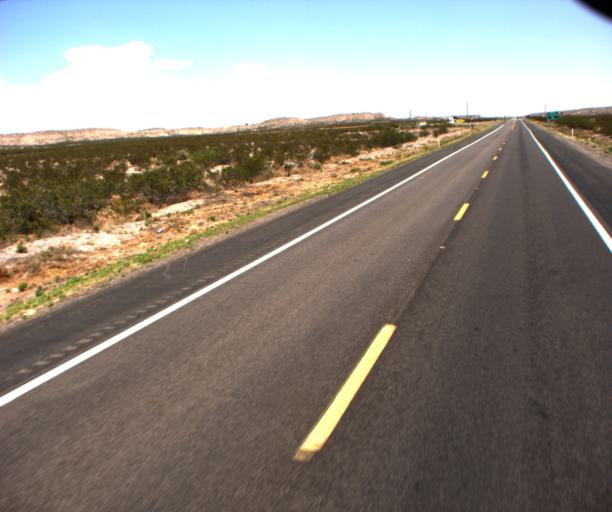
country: US
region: Arizona
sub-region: Greenlee County
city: Clifton
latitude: 32.6579
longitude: -109.0668
